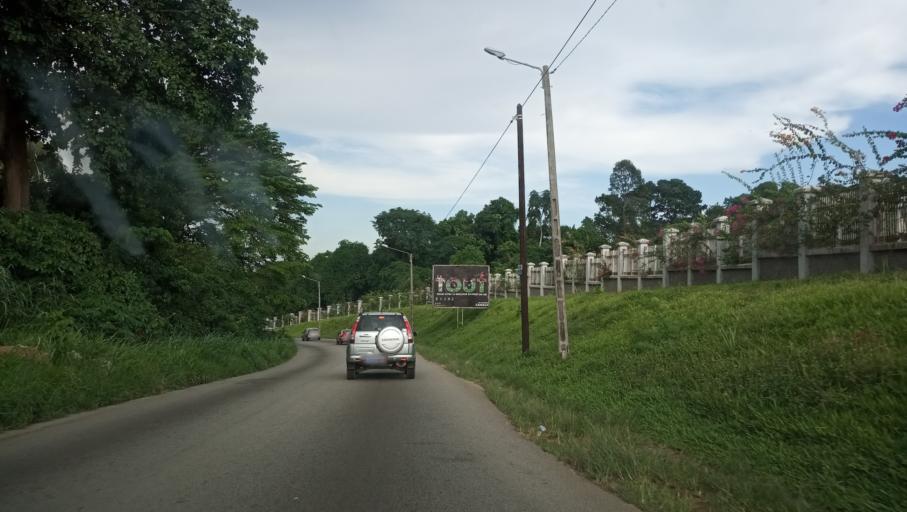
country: CI
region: Lagunes
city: Abidjan
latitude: 5.3495
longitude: -3.9856
